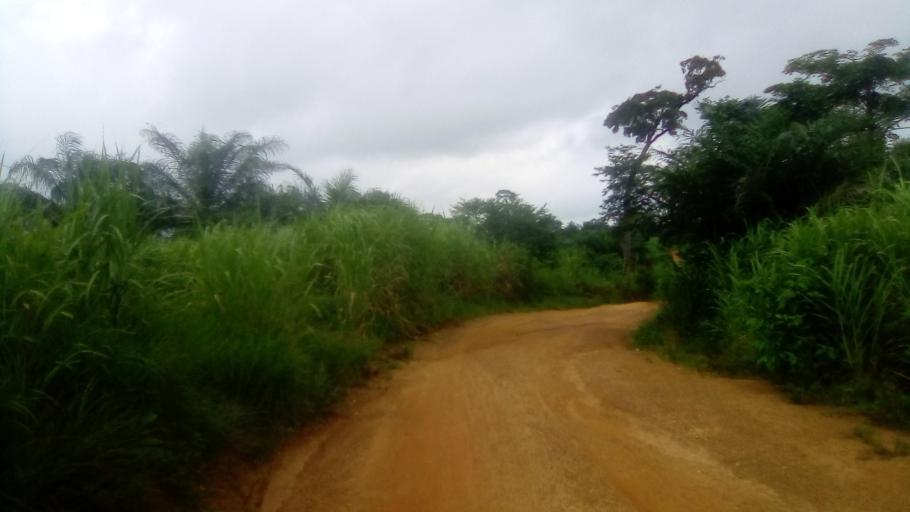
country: SL
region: Eastern Province
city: Kailahun
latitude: 8.3022
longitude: -10.5593
